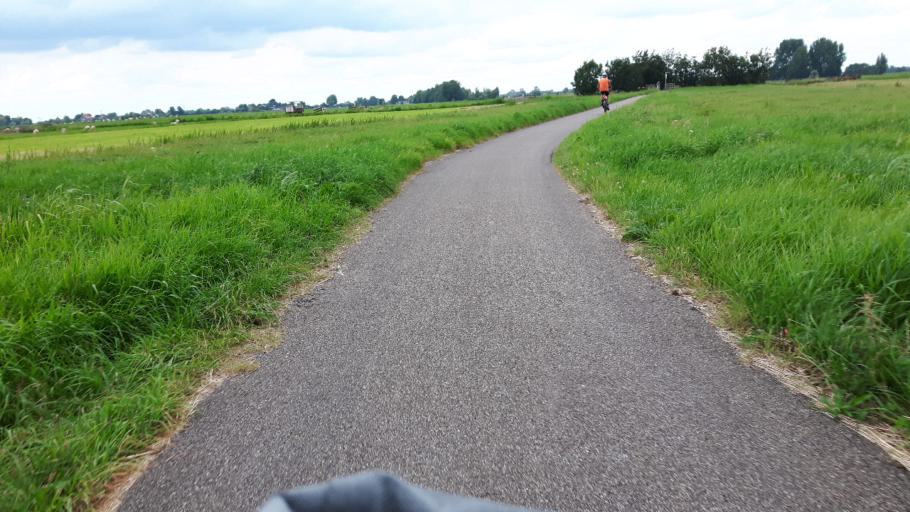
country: NL
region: South Holland
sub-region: Gemeente Vlist
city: Haastrecht
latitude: 51.9484
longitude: 4.7431
